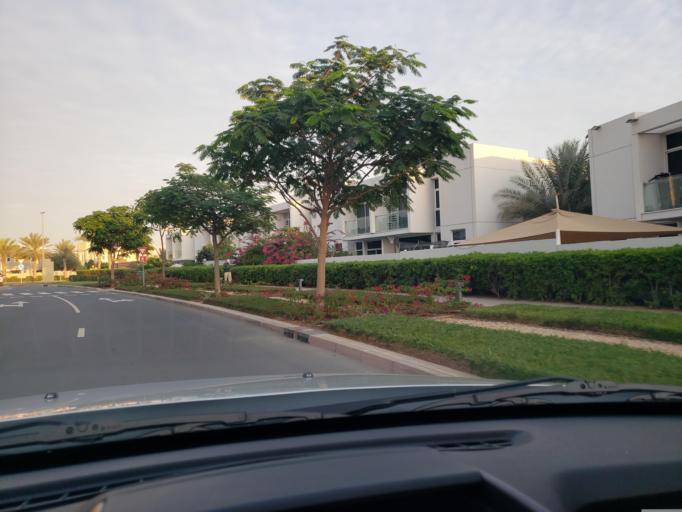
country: AE
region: Dubai
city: Dubai
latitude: 25.0197
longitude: 55.2729
